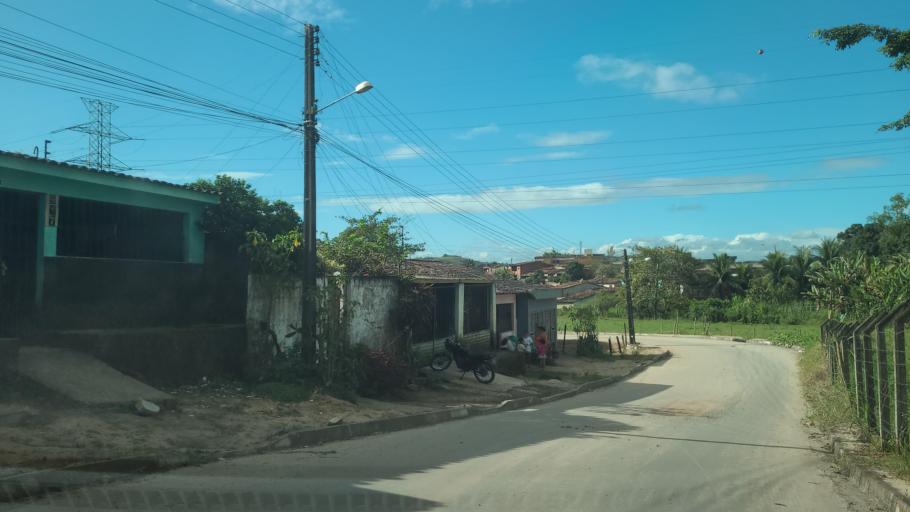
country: BR
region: Alagoas
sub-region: Uniao Dos Palmares
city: Uniao dos Palmares
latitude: -9.1601
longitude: -36.0161
